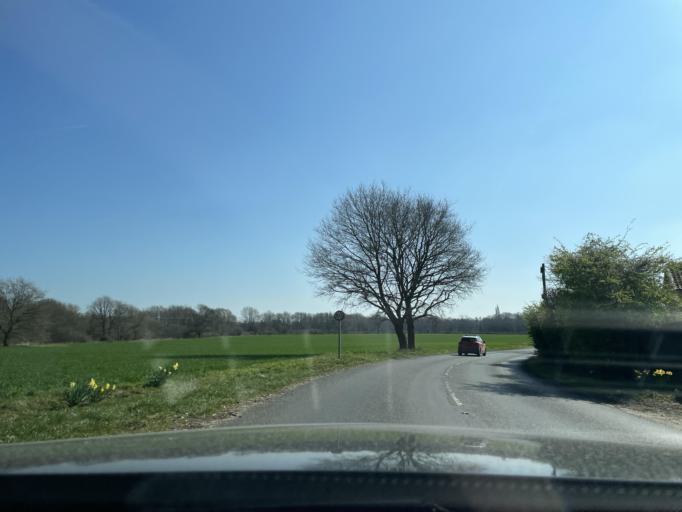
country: GB
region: England
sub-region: Norfolk
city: Hingham
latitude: 52.6151
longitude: 1.0133
